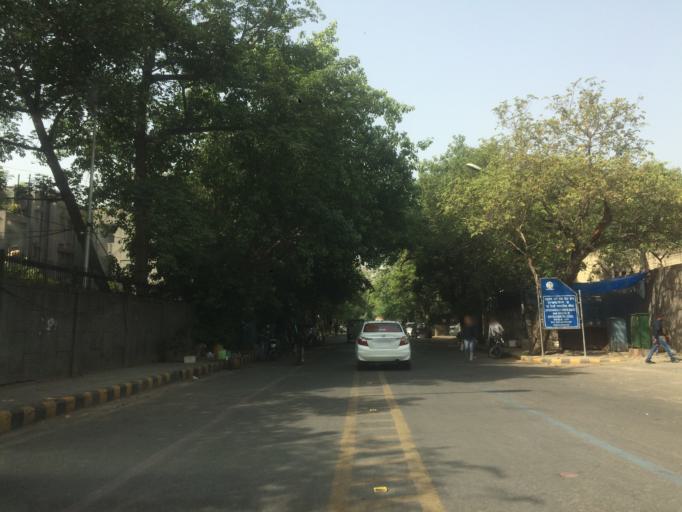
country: IN
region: NCT
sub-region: Central Delhi
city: Karol Bagh
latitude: 28.6328
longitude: 77.2017
